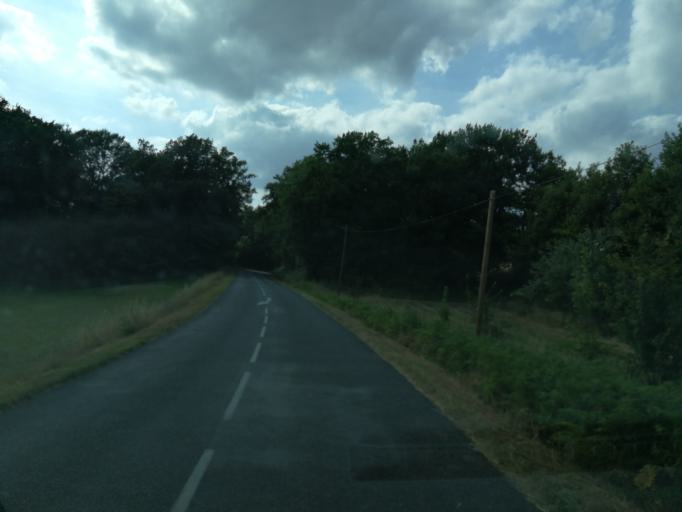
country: FR
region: Aquitaine
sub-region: Departement du Lot-et-Garonne
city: Monsempron-Libos
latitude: 44.5286
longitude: 0.9364
